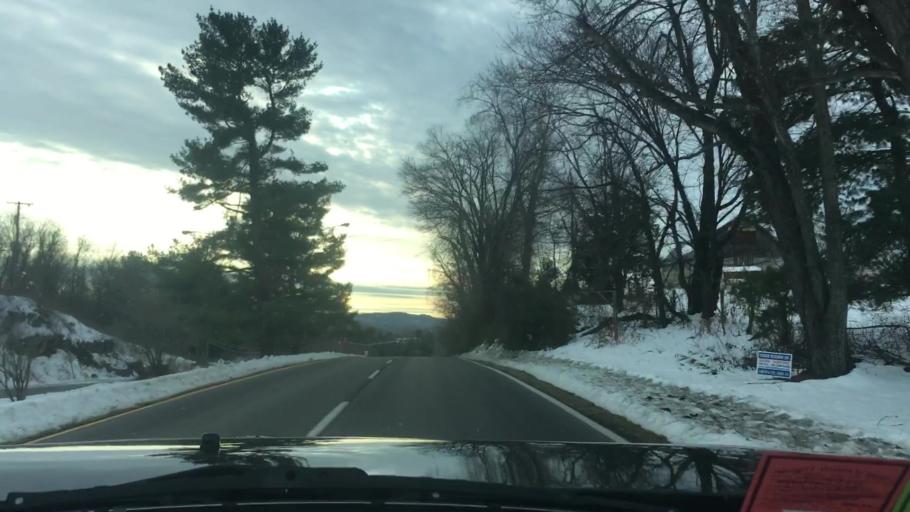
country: US
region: Virginia
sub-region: Pulaski County
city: Pulaski
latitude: 37.0658
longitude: -80.7635
